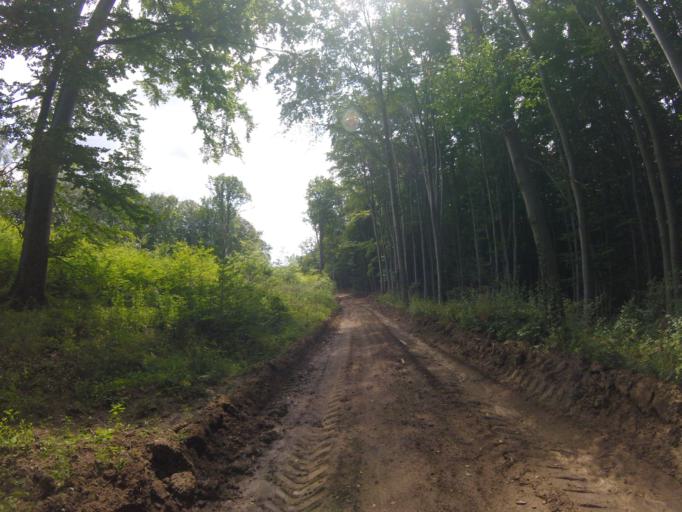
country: SK
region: Nitriansky
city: Sahy
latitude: 47.9535
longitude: 18.8895
